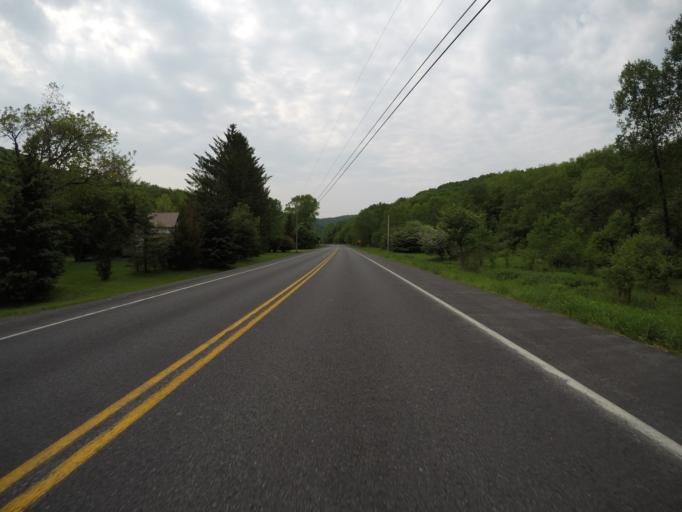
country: US
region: New York
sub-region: Sullivan County
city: Livingston Manor
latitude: 41.9844
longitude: -74.8948
